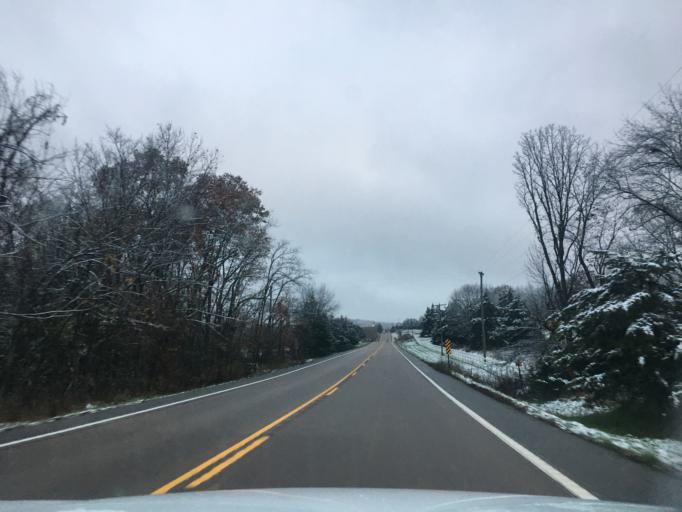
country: US
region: Missouri
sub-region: Osage County
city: Linn
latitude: 38.4692
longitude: -91.7633
